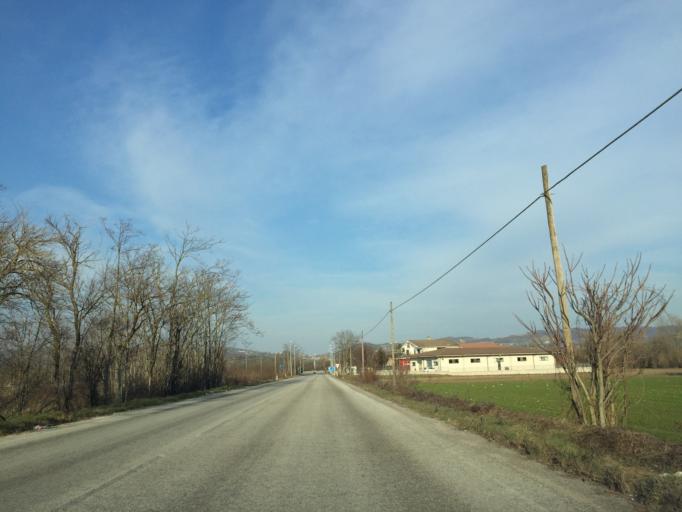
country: IT
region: Molise
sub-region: Provincia di Campobasso
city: San Massimo
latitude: 41.5085
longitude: 14.4327
